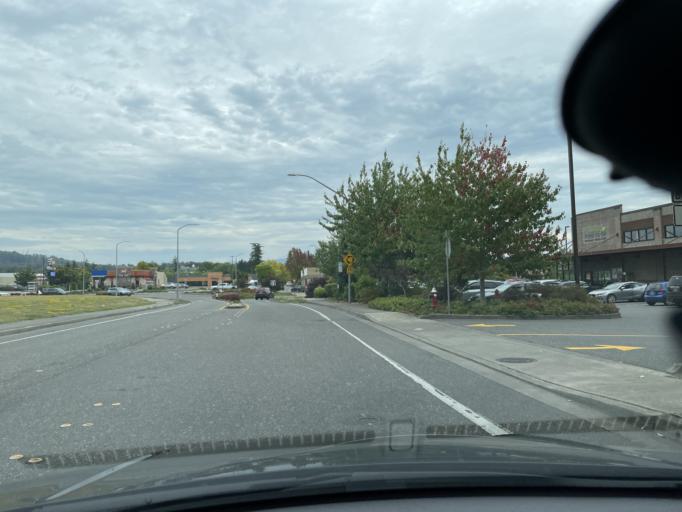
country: US
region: Washington
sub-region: Whatcom County
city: Bellingham
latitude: 48.7920
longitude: -122.4929
